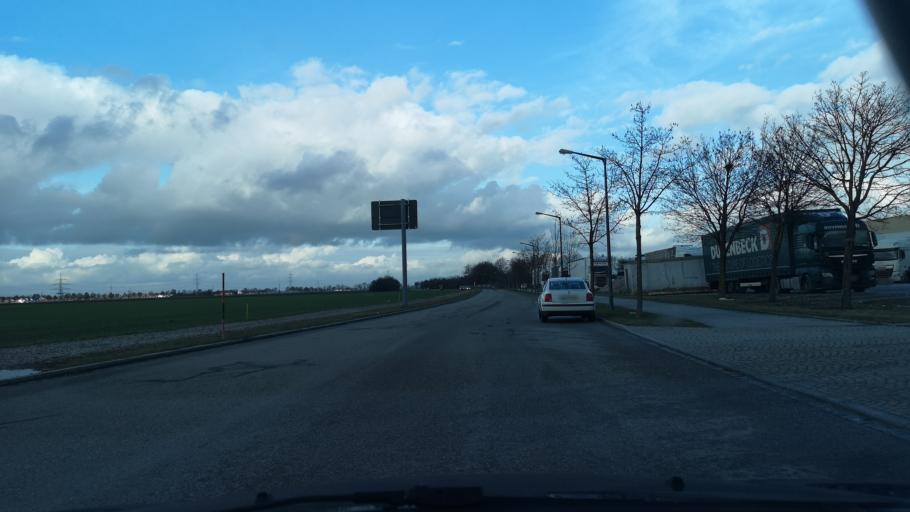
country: DE
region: Bavaria
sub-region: Upper Bavaria
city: Poing
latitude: 48.1689
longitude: 11.7916
